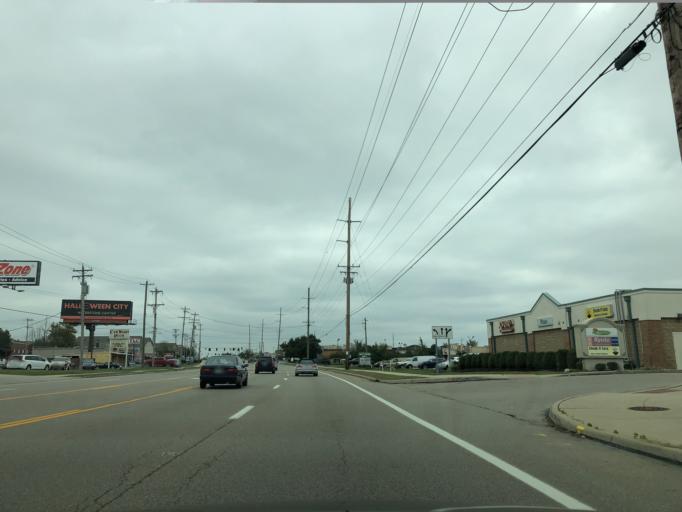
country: US
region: Ohio
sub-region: Warren County
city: Landen
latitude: 39.2889
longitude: -84.3018
